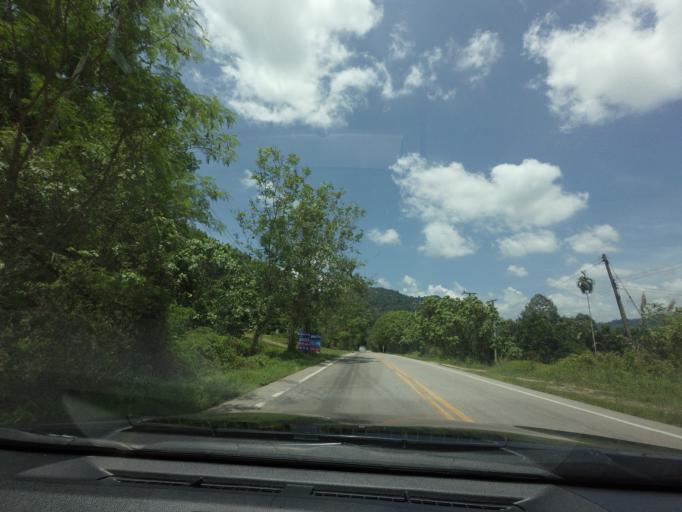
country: TH
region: Chumphon
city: Ban Nam Yuen
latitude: 9.9093
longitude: 98.9127
